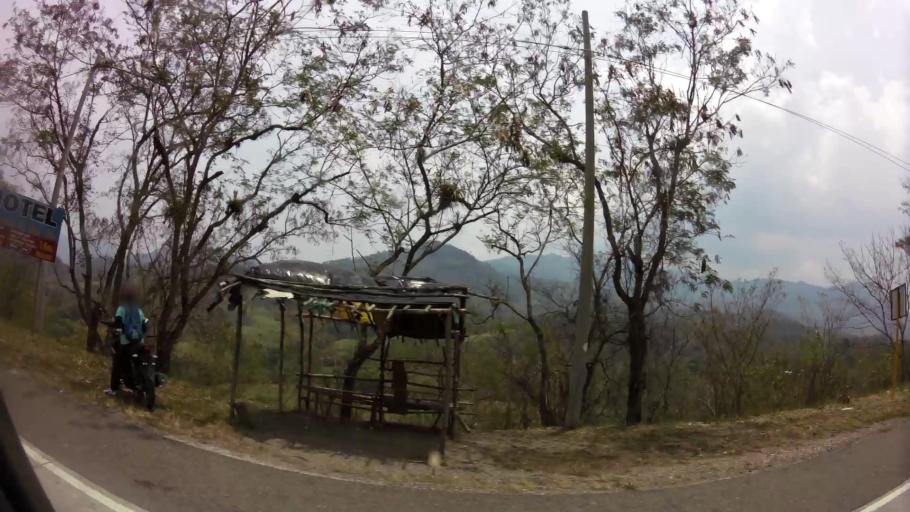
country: HN
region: Comayagua
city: Taulabe
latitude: 14.6943
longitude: -87.9467
